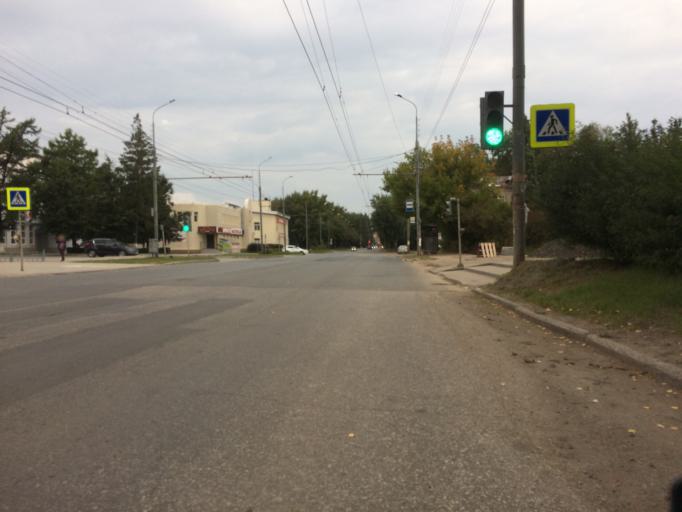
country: RU
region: Mariy-El
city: Yoshkar-Ola
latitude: 56.6341
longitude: 47.8677
